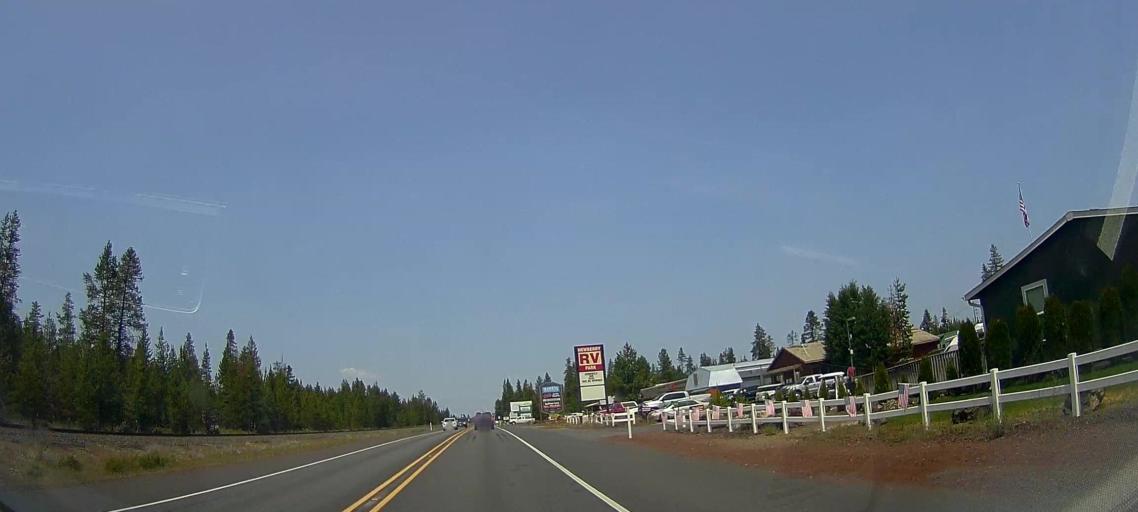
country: US
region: Oregon
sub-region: Deschutes County
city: La Pine
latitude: 43.7122
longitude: -121.4742
